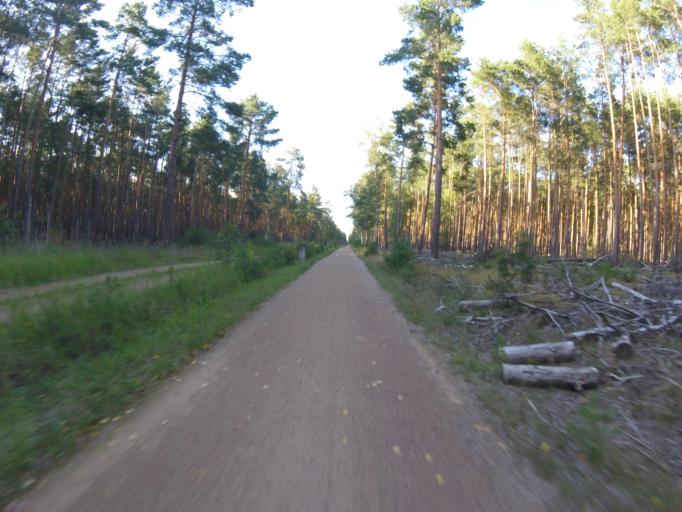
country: DE
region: Brandenburg
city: Halbe
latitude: 52.1862
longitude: 13.7591
